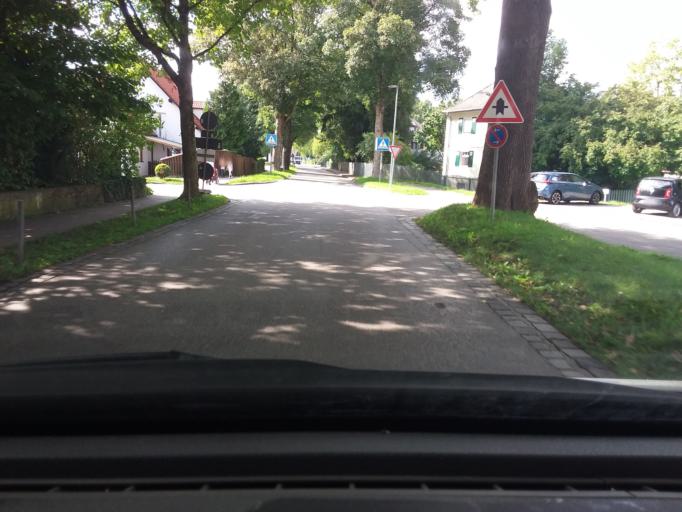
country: DE
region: Bavaria
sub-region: Upper Bavaria
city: Ismaning
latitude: 48.2261
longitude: 11.6817
